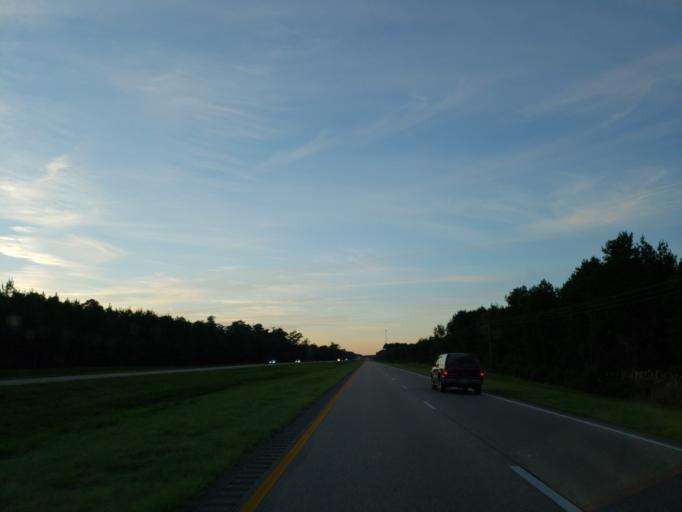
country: US
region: Mississippi
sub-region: Wayne County
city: Belmont
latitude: 31.6044
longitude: -88.5609
